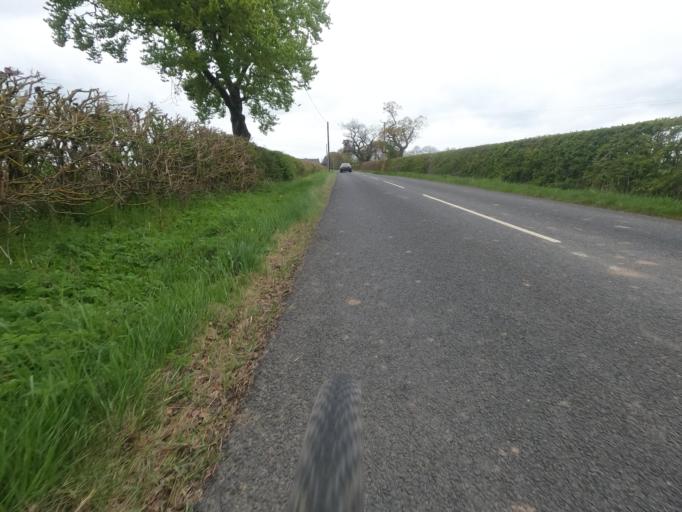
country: GB
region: England
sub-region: Northumberland
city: Darras Hall
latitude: 55.0522
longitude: -1.7703
